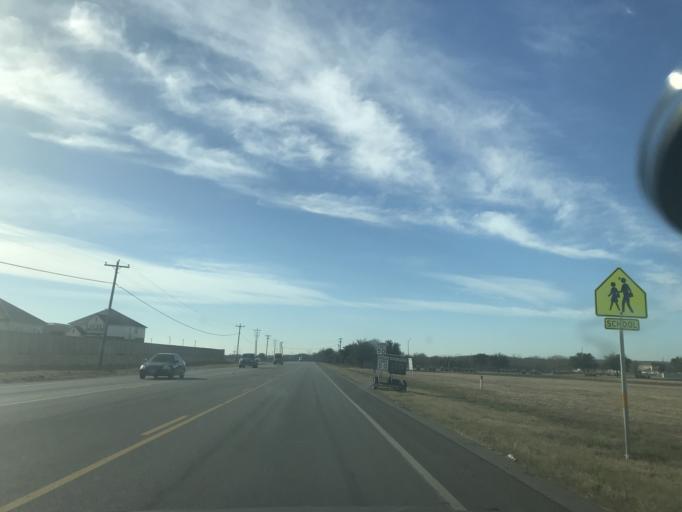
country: US
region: Texas
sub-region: Travis County
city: Manor
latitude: 30.3338
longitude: -97.5595
